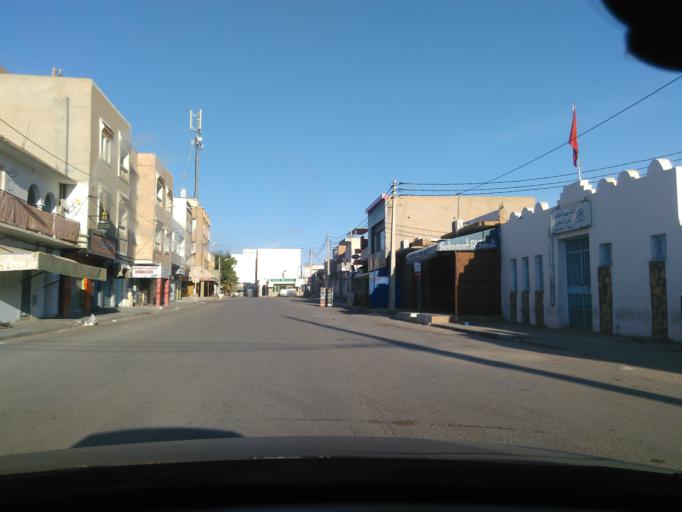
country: TN
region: Tataouine
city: Tataouine
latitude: 32.9296
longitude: 10.4472
